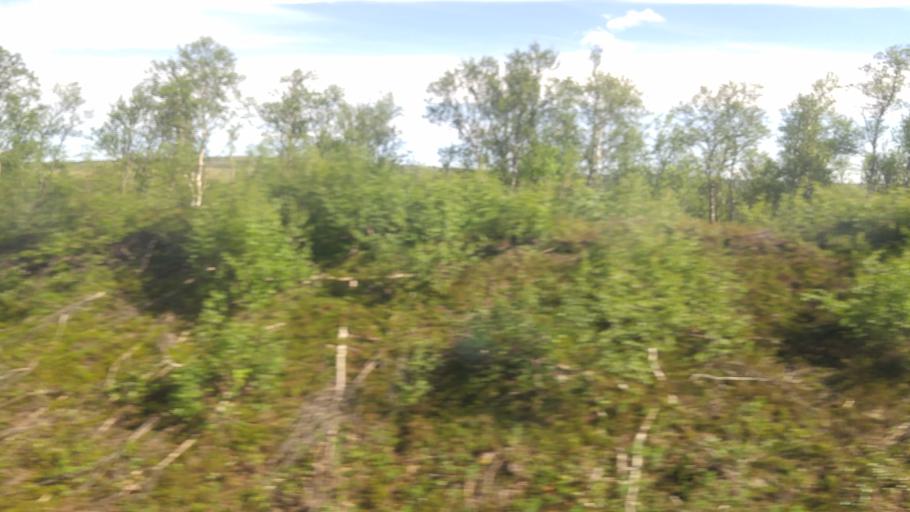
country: NO
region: Nord-Trondelag
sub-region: Meraker
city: Meraker
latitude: 63.3197
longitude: 12.1730
